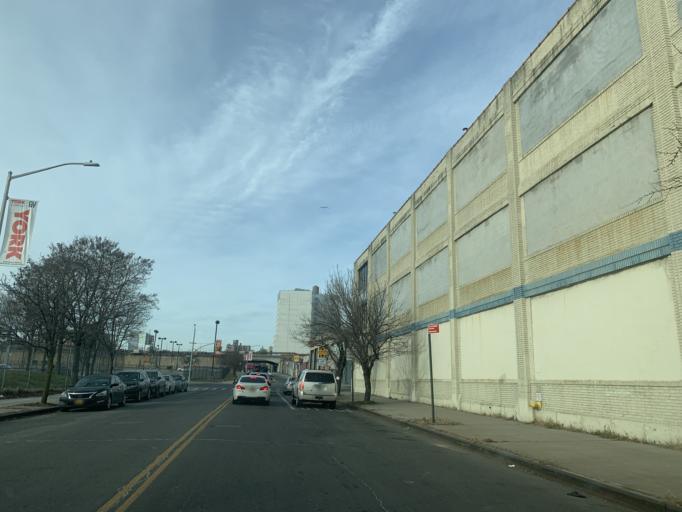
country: US
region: New York
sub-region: Queens County
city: Jamaica
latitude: 40.7016
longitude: -73.7920
